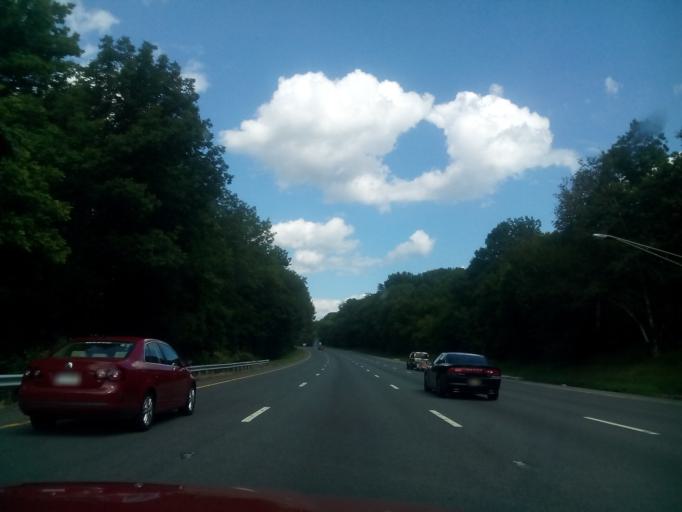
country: US
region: New Jersey
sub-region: Warren County
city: Belvidere
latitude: 40.9303
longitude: -75.0336
